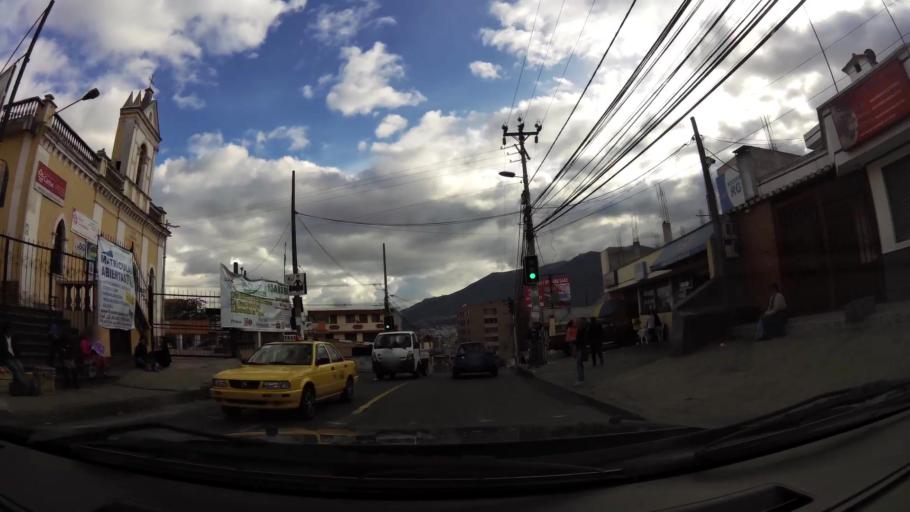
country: EC
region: Pichincha
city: Quito
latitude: -0.1484
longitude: -78.4665
